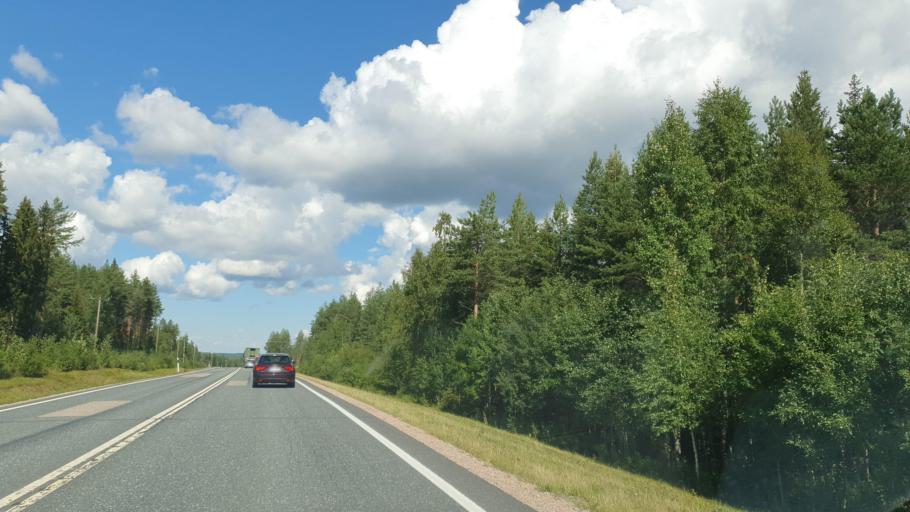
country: FI
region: Kainuu
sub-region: Kajaani
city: Kajaani
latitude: 64.0922
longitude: 27.4526
